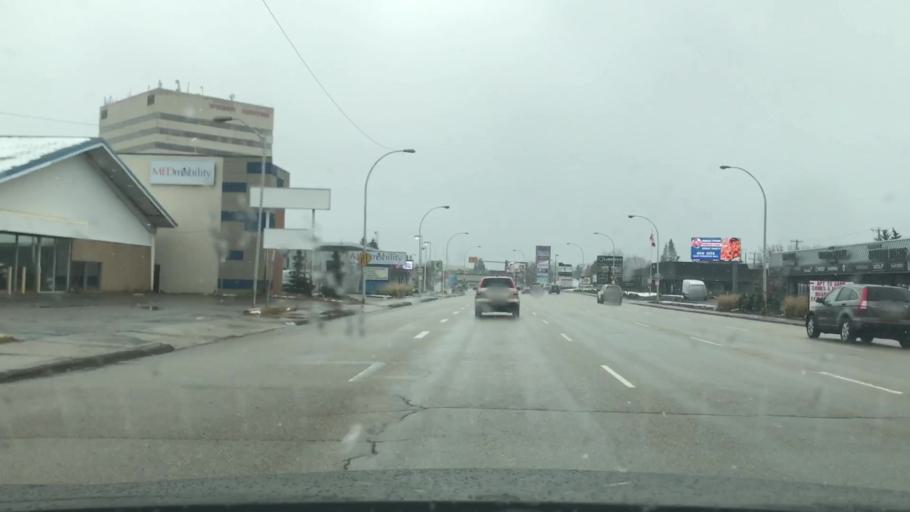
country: CA
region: Alberta
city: Edmonton
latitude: 53.4951
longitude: -113.4976
